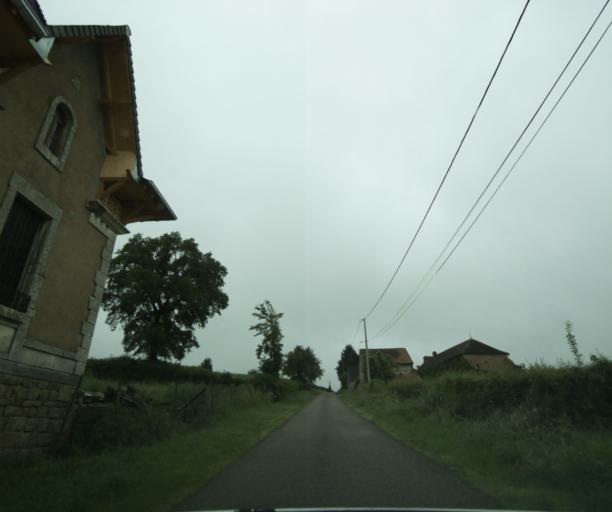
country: FR
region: Bourgogne
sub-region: Departement de Saone-et-Loire
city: Charolles
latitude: 46.4323
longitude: 4.4130
